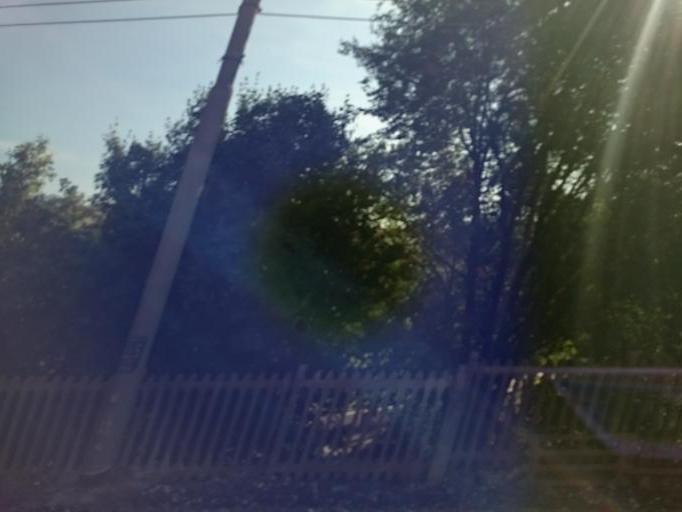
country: IT
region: Veneto
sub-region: Provincia di Verona
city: Sant'Ambrogio di Valpollicella
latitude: 45.5153
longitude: 10.8240
